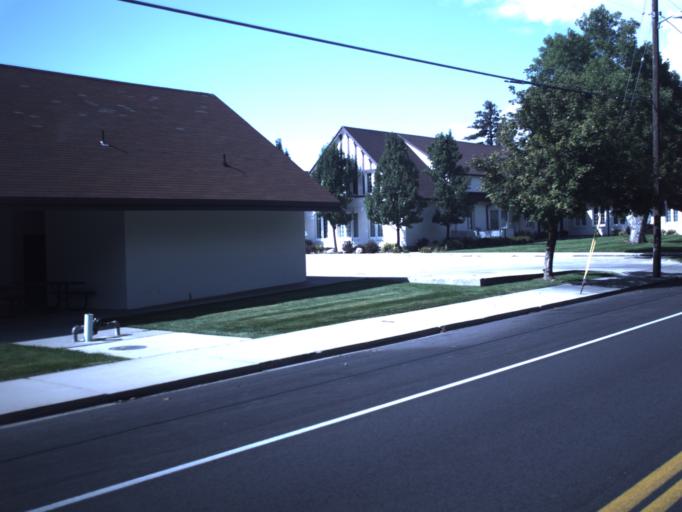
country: US
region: Utah
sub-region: Utah County
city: Mapleton
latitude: 40.1293
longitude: -111.5788
